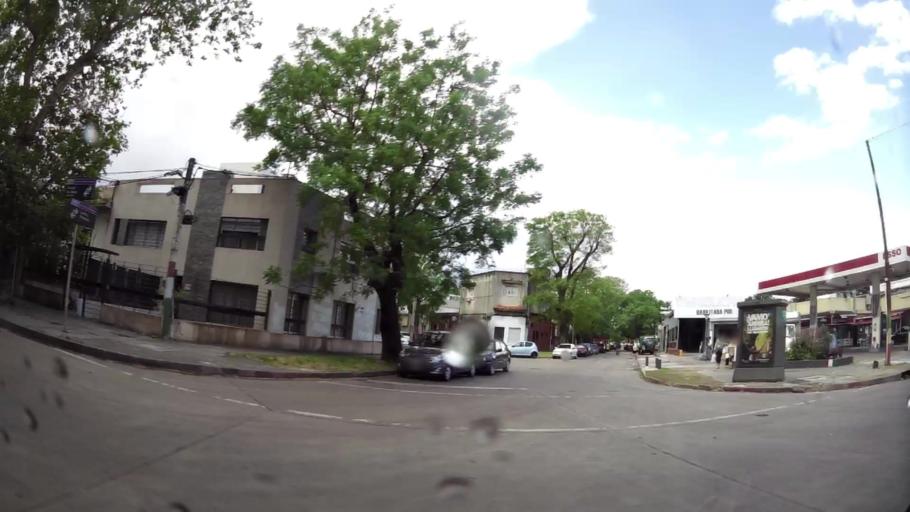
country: UY
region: Montevideo
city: Montevideo
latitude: -34.8686
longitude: -56.1813
